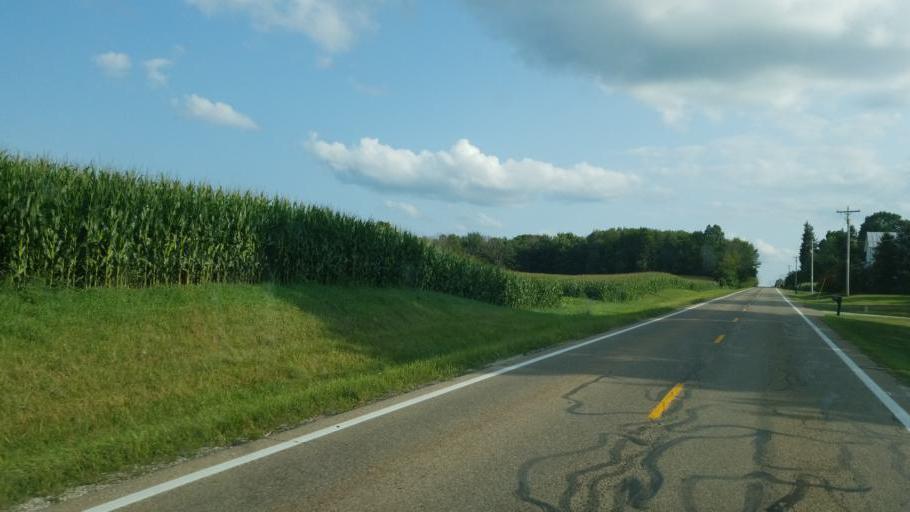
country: US
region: Ohio
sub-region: Richland County
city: Lexington
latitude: 40.6999
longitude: -82.6654
